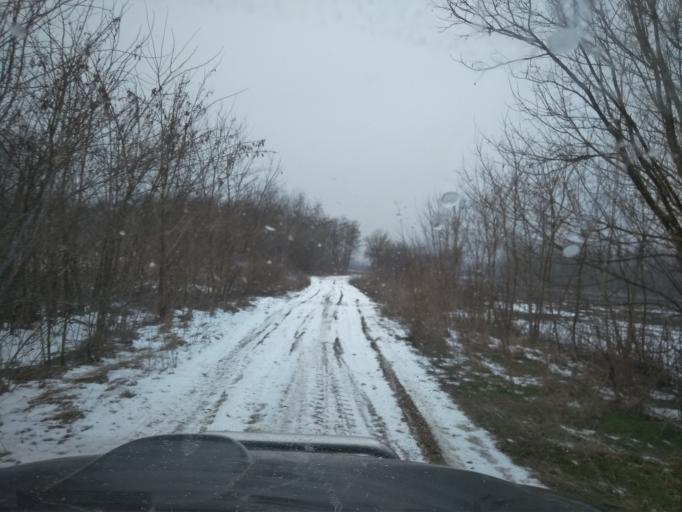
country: HU
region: Szabolcs-Szatmar-Bereg
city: Apagy
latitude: 47.9743
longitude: 21.9170
